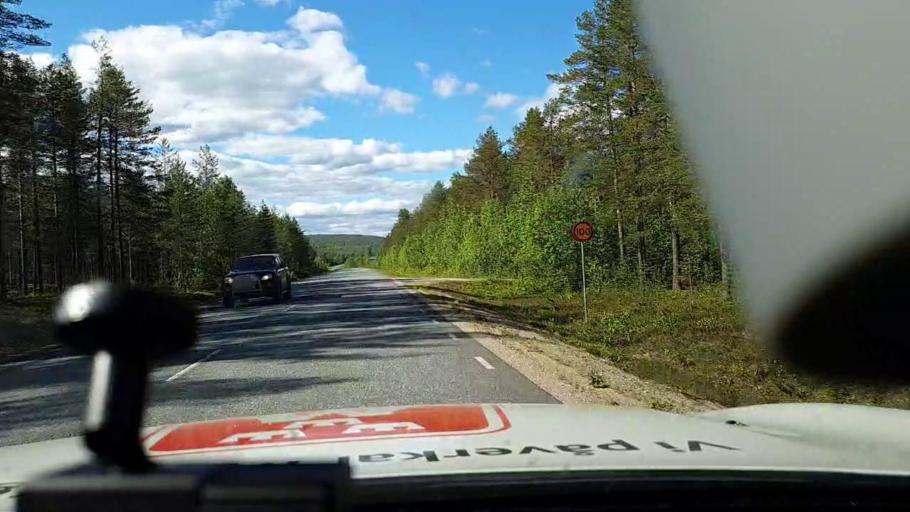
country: FI
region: Lapland
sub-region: Torniolaakso
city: Ylitornio
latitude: 66.2965
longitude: 23.6370
